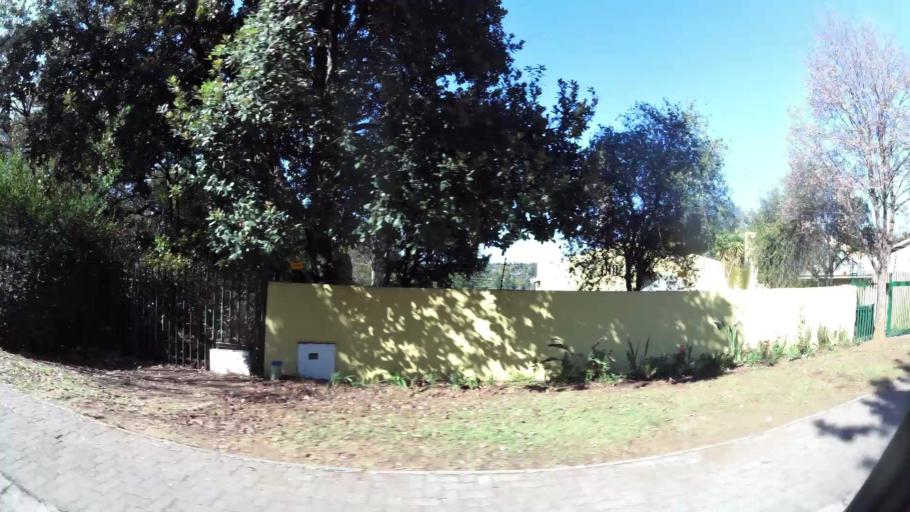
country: ZA
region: Gauteng
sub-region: City of Johannesburg Metropolitan Municipality
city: Roodepoort
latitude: -26.1094
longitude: 27.9609
